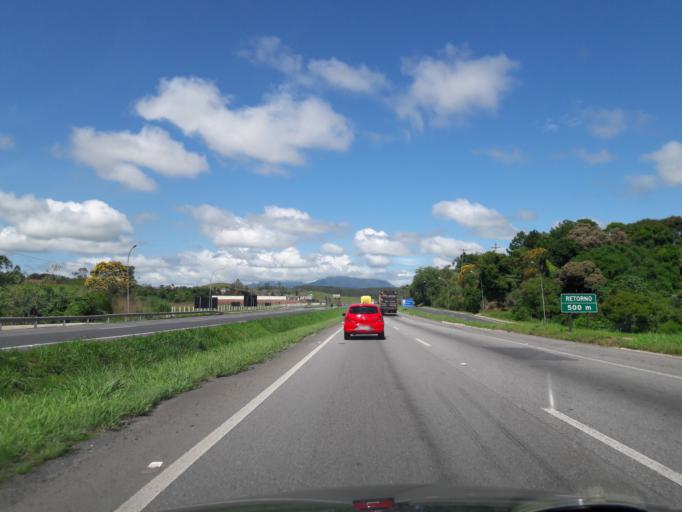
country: BR
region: Sao Paulo
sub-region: Jacupiranga
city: Jacupiranga
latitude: -24.7050
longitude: -48.0125
